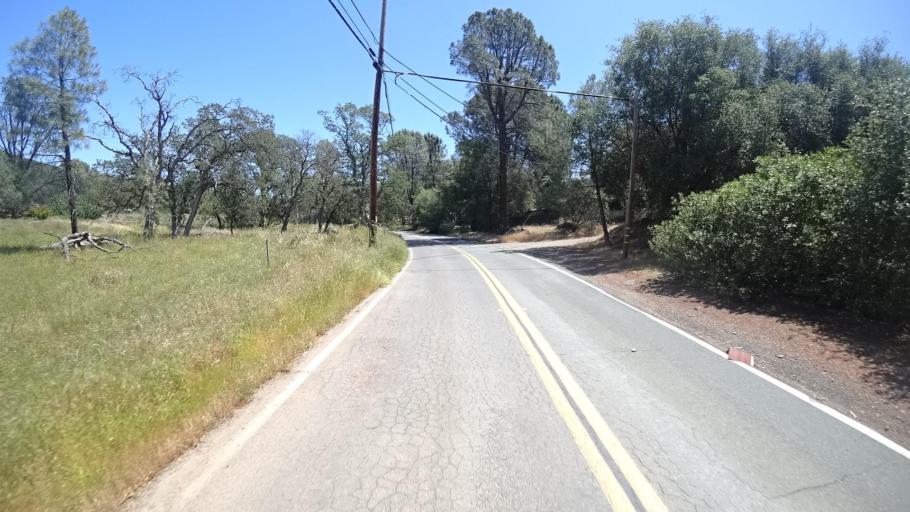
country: US
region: California
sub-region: Lake County
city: Hidden Valley Lake
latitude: 38.8212
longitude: -122.5595
